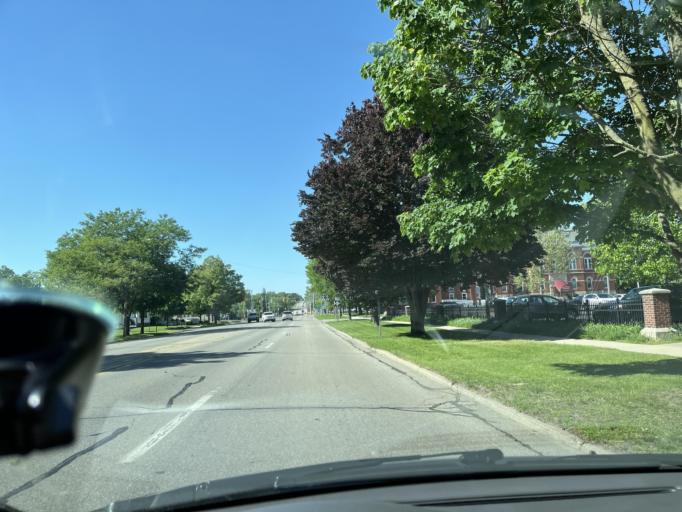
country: US
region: Michigan
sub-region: Barry County
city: Hastings
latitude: 42.6470
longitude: -85.2906
